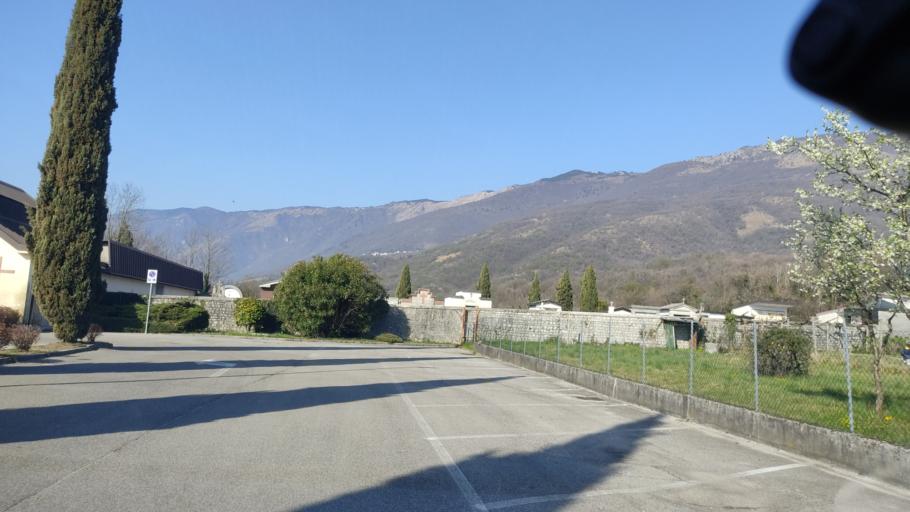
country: IT
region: Friuli Venezia Giulia
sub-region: Provincia di Pordenone
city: Budoia
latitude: 46.0512
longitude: 12.5328
